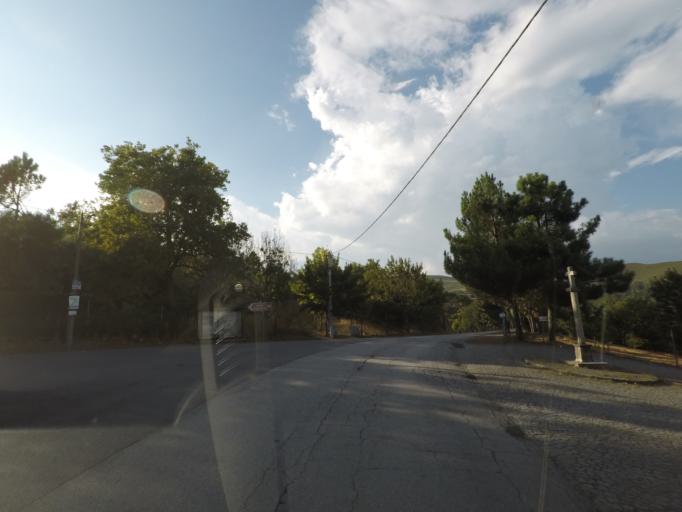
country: PT
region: Porto
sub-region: Baiao
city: Valadares
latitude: 41.1715
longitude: -7.9420
